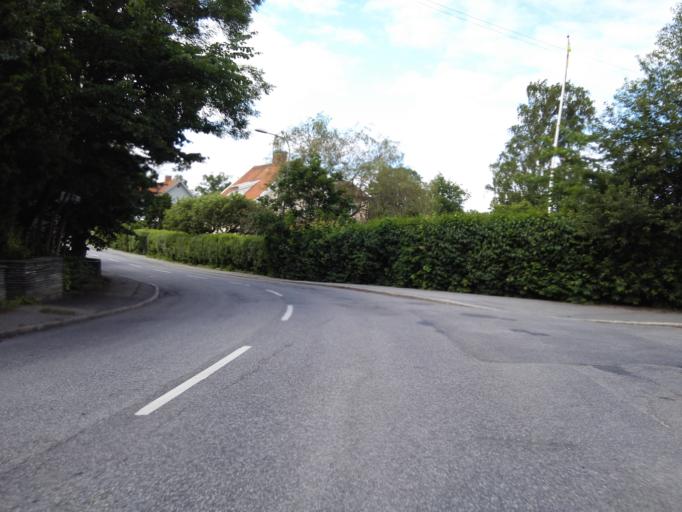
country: SE
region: Stockholm
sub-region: Huddinge Kommun
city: Huddinge
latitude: 59.2718
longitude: 17.9871
